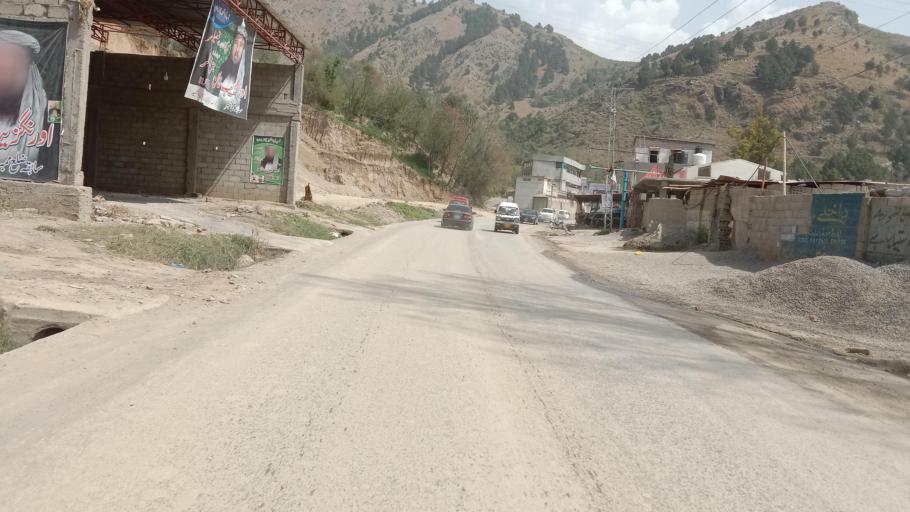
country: PK
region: Khyber Pakhtunkhwa
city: Abbottabad
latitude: 34.1450
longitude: 73.2675
